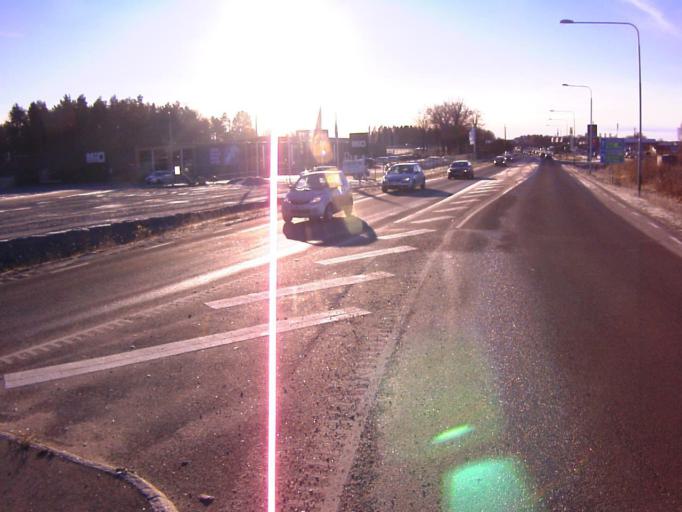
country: SE
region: Soedermanland
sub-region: Eskilstuna Kommun
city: Torshalla
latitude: 59.3962
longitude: 16.4696
